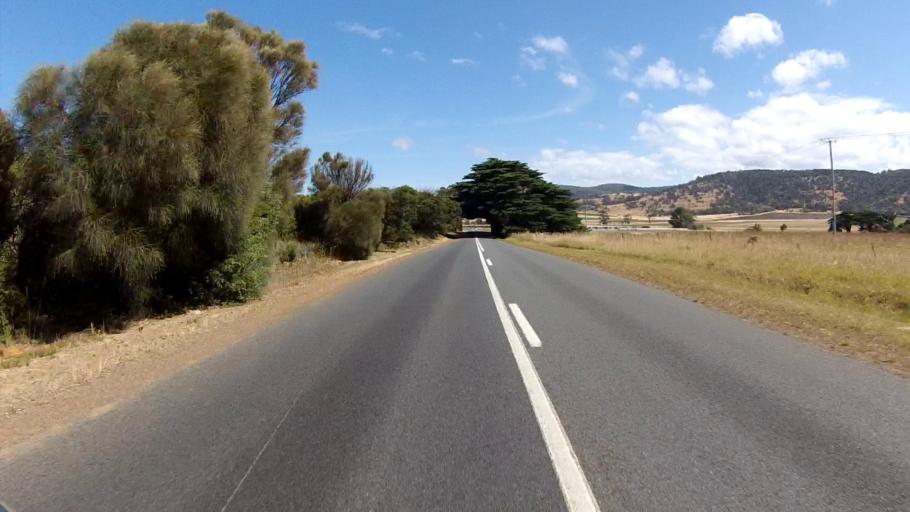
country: AU
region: Tasmania
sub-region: Sorell
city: Sorell
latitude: -42.1992
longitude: 148.0480
